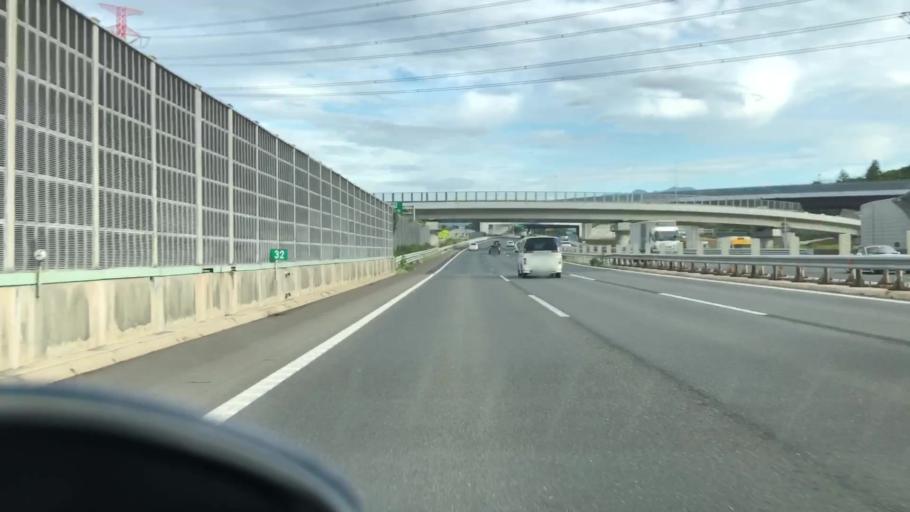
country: JP
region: Hyogo
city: Sandacho
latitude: 34.8516
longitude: 135.2210
